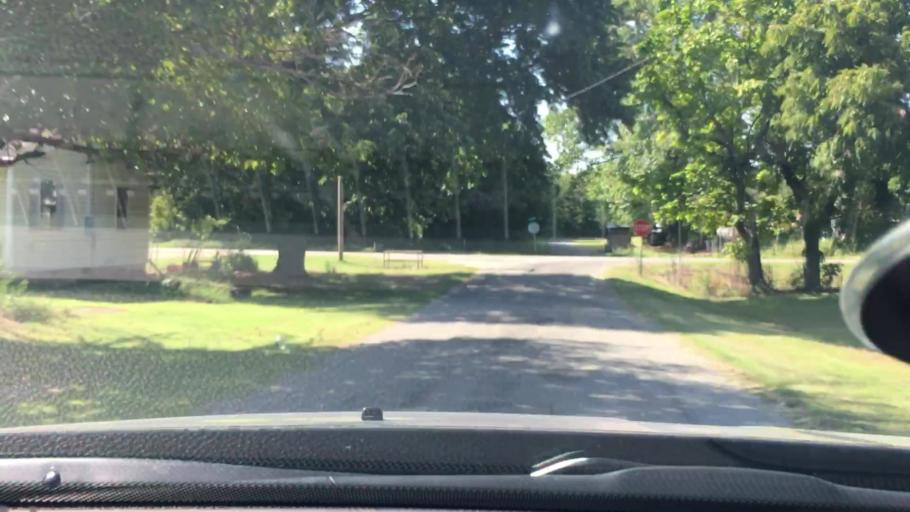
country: US
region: Oklahoma
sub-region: Johnston County
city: Tishomingo
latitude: 34.2409
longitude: -96.5525
